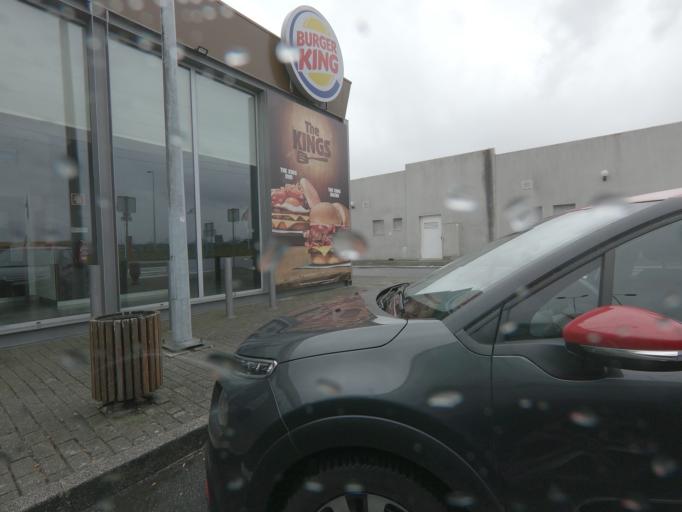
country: PT
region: Porto
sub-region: Matosinhos
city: Senhora da Hora
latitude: 41.2046
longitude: -8.6398
